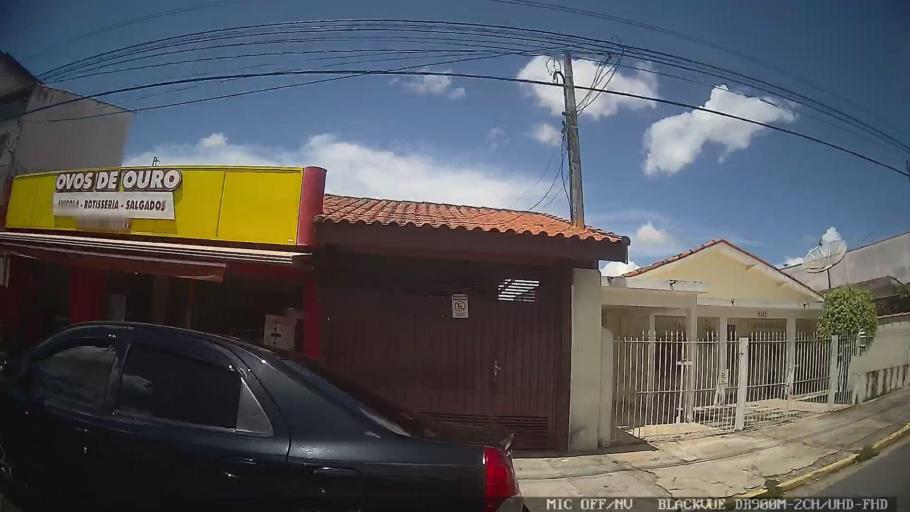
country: BR
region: Sao Paulo
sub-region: Atibaia
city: Atibaia
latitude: -23.1256
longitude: -46.5640
